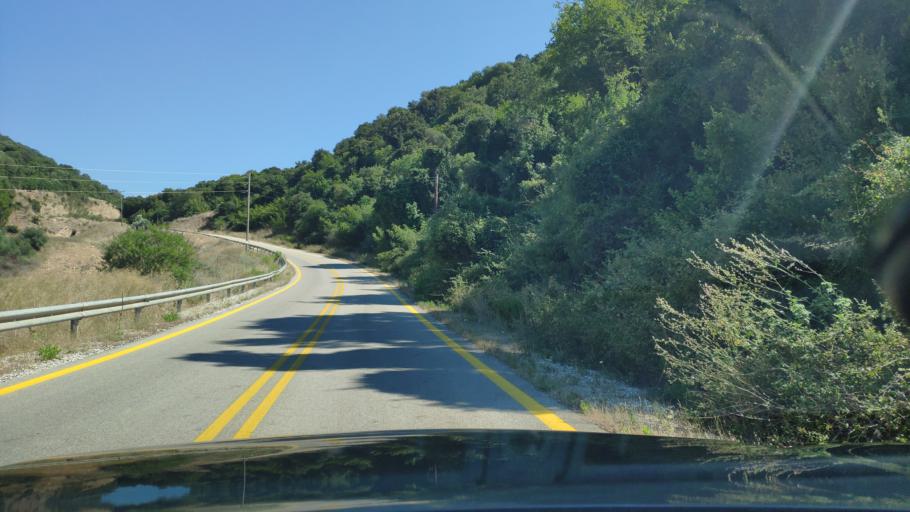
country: GR
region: West Greece
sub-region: Nomos Aitolias kai Akarnanias
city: Amfilochia
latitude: 38.8613
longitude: 21.0824
